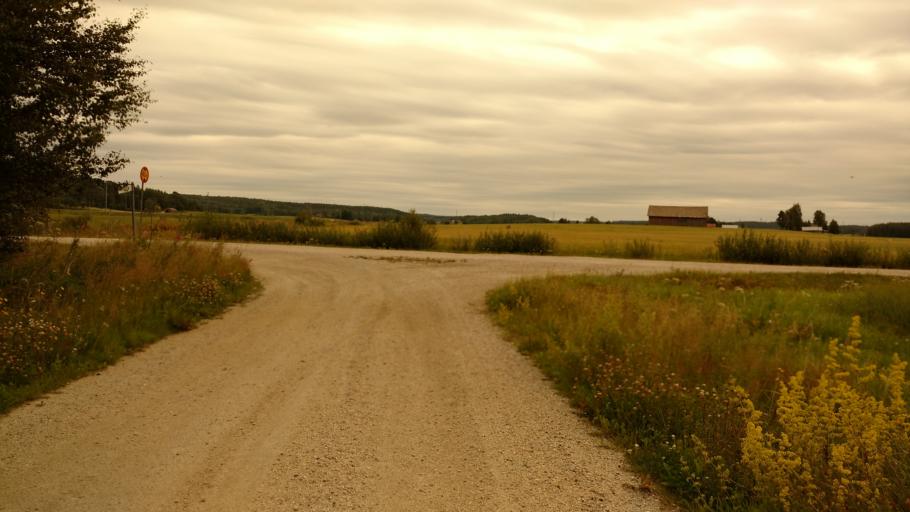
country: FI
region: Varsinais-Suomi
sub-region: Turku
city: Paimio
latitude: 60.4190
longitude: 22.8341
